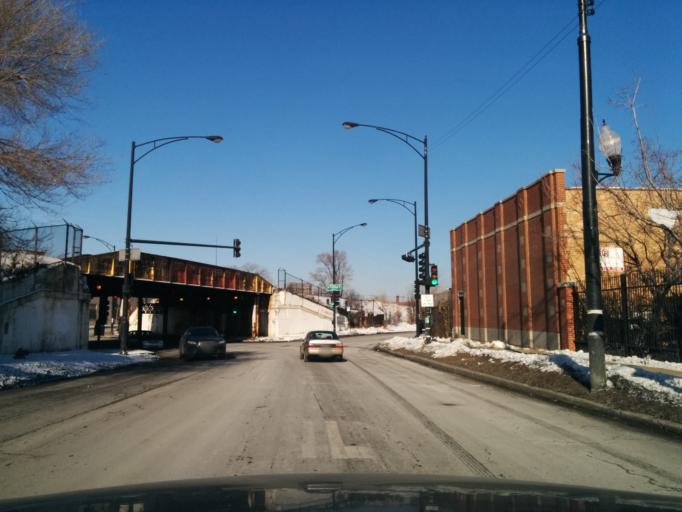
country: US
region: Illinois
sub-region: Cook County
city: Cicero
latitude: 41.9001
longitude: -87.7109
